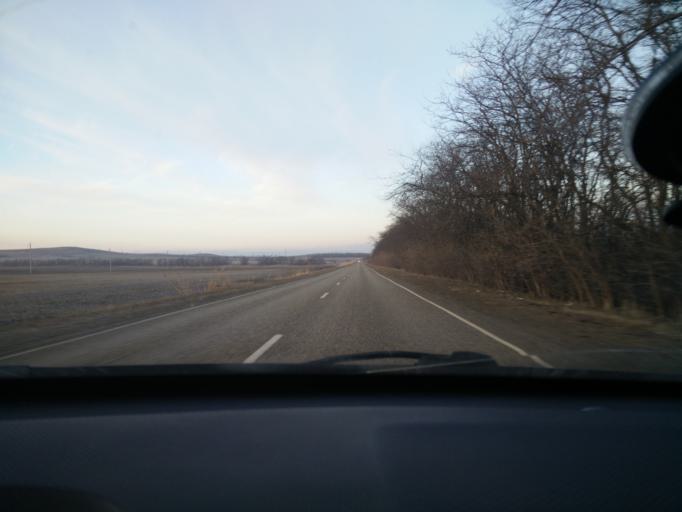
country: RU
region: Stavropol'skiy
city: Tatarka
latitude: 44.9952
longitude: 41.7322
